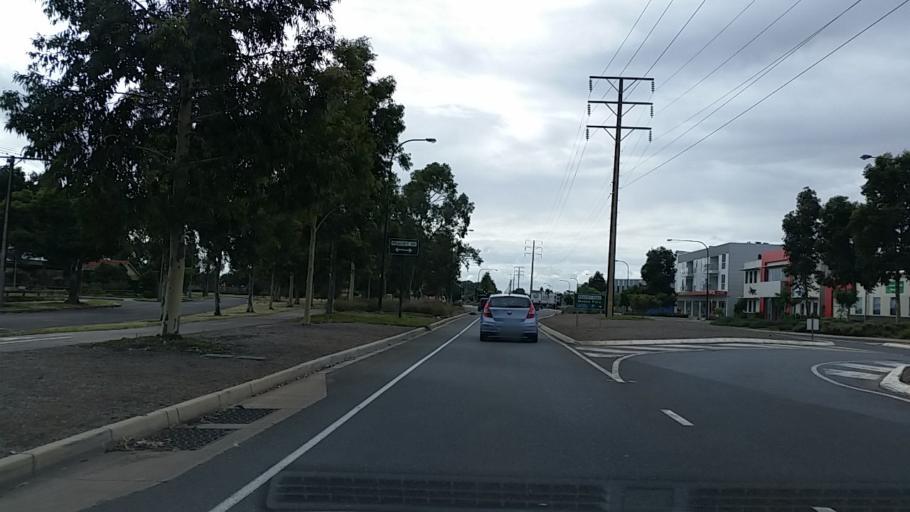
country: AU
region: South Australia
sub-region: Playford
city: Smithfield
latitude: -34.6727
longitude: 138.6810
